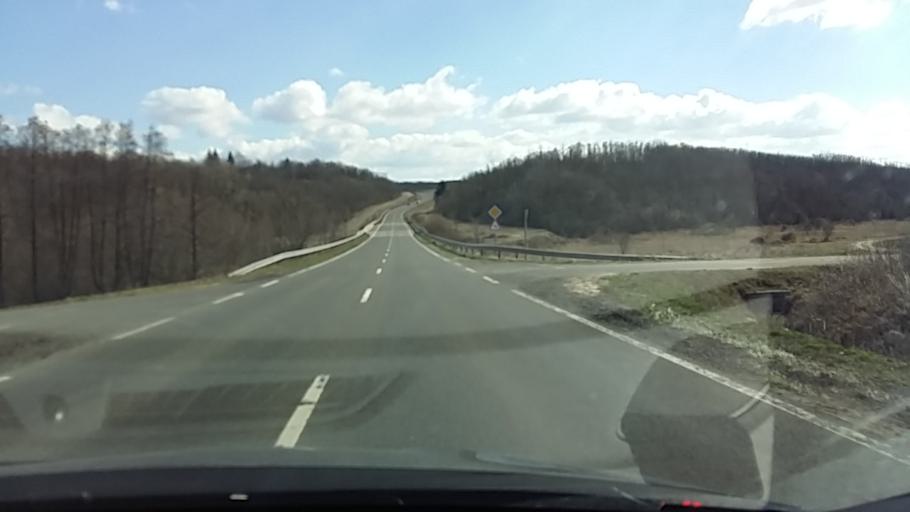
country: HU
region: Baranya
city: Kozarmisleny
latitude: 46.0282
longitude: 18.2774
